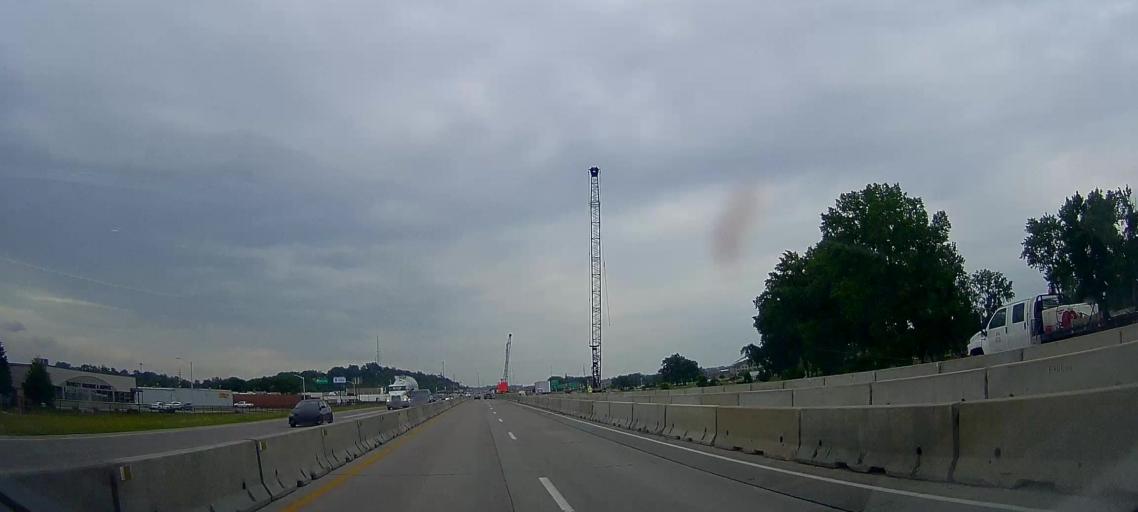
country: US
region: Nebraska
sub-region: Dakota County
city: South Sioux City
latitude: 42.4918
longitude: -96.4299
